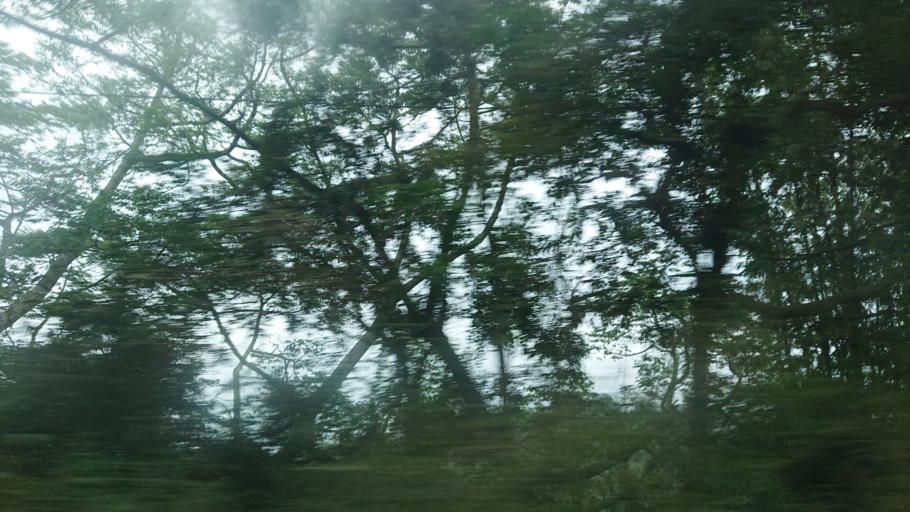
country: TW
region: Taiwan
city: Lugu
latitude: 23.5916
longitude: 120.7128
